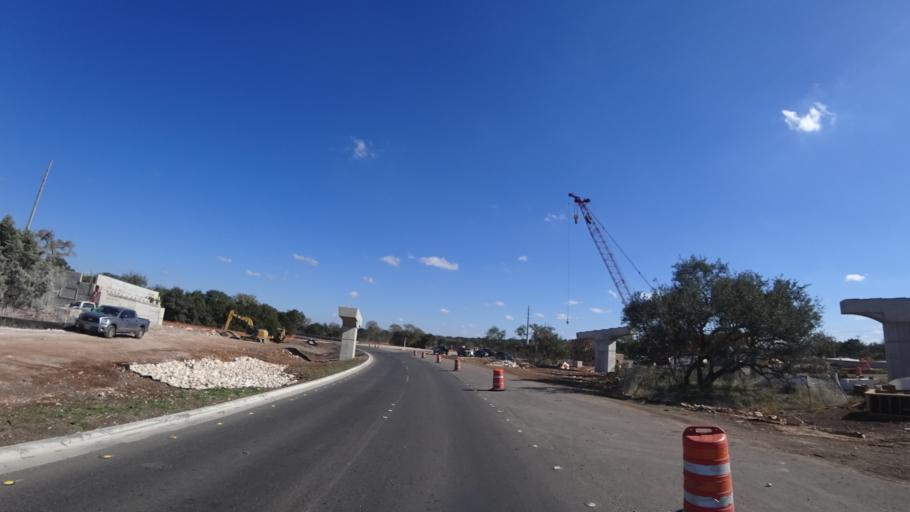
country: US
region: Texas
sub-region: Travis County
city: Shady Hollow
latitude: 30.1734
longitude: -97.8893
